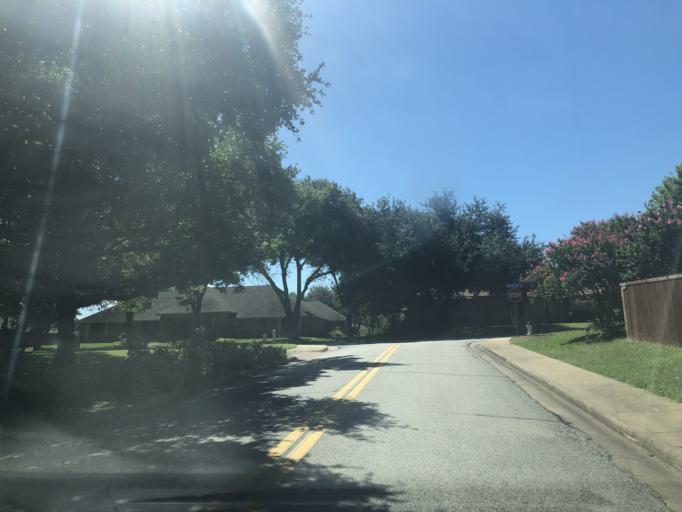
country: US
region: Texas
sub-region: Dallas County
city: Duncanville
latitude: 32.6351
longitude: -96.9298
